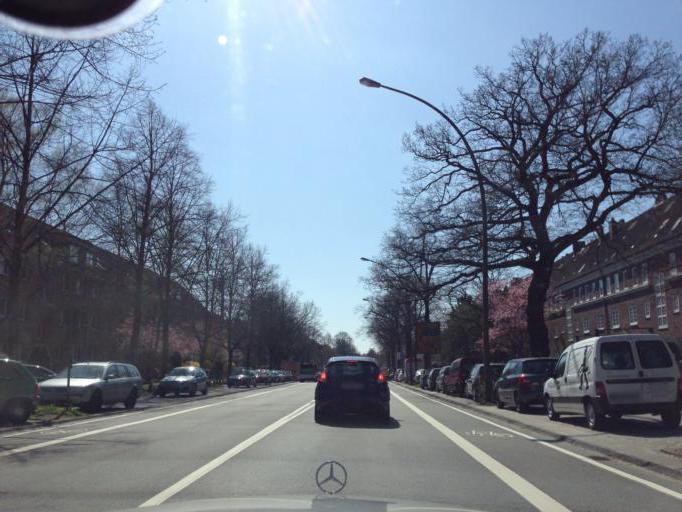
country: DE
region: Hamburg
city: Fuhlsbuettel
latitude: 53.6257
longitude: 10.0124
